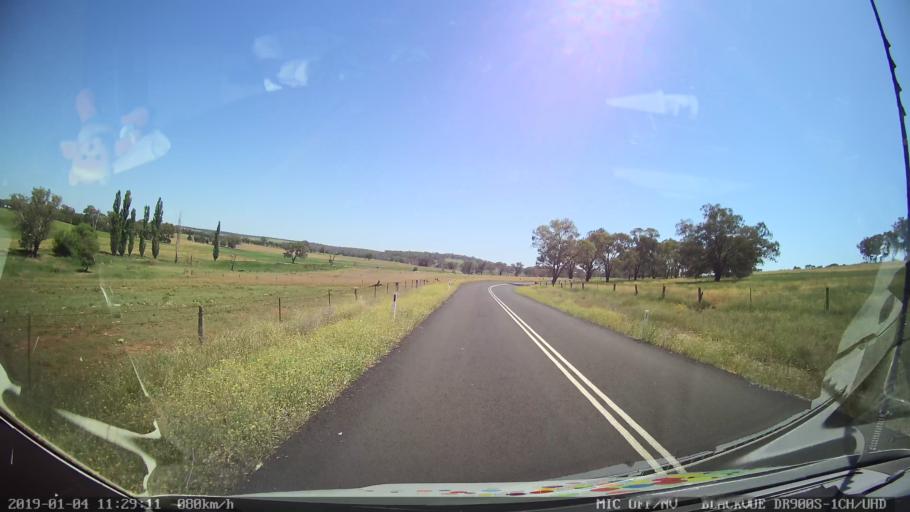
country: AU
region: New South Wales
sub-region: Cabonne
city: Molong
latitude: -33.0907
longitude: 148.7731
